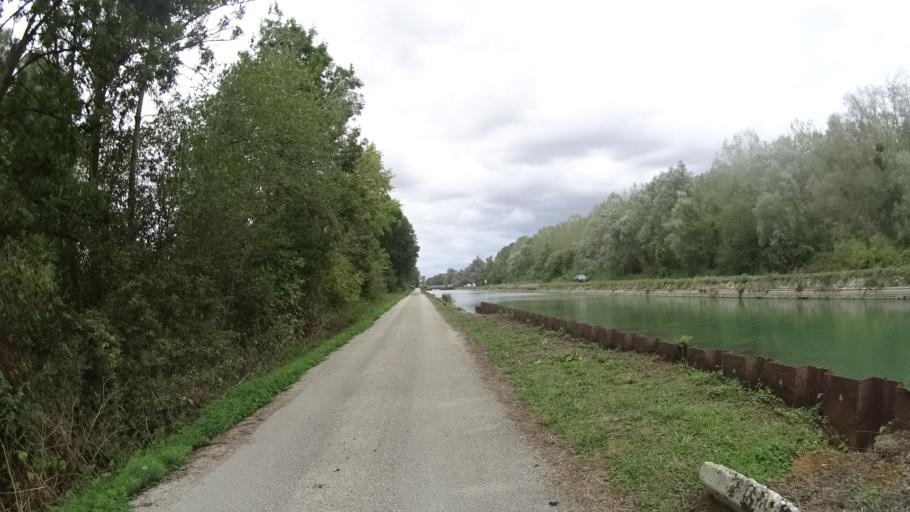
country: FR
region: Picardie
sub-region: Departement de l'Aisne
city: La Fere
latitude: 49.6871
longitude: 3.3658
